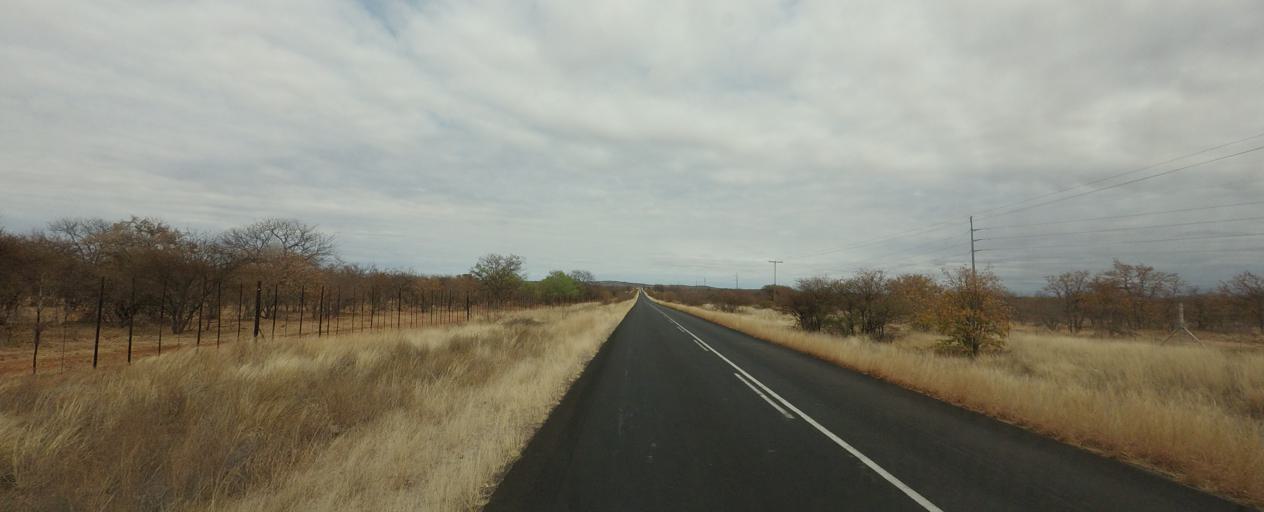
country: ZW
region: Matabeleland South
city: Beitbridge
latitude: -22.4316
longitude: 29.4681
